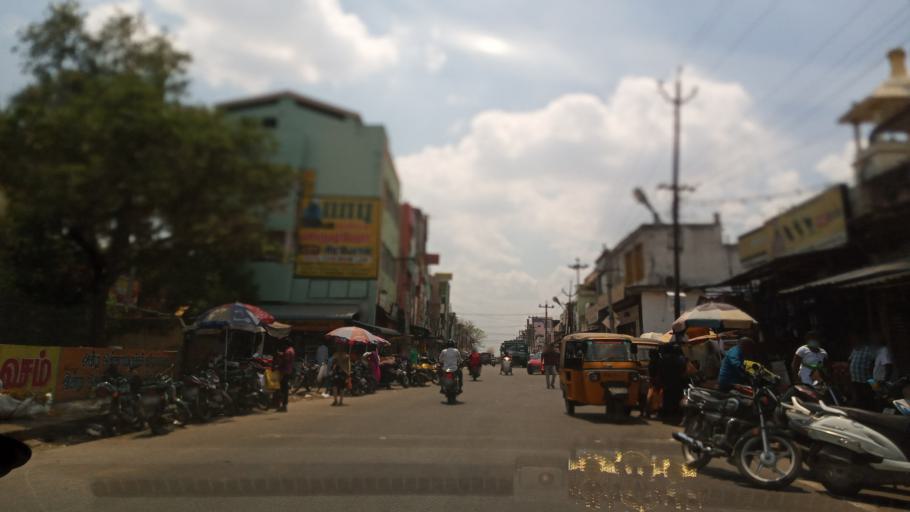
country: IN
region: Tamil Nadu
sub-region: Vellore
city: Walajapet
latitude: 12.9253
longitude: 79.3648
